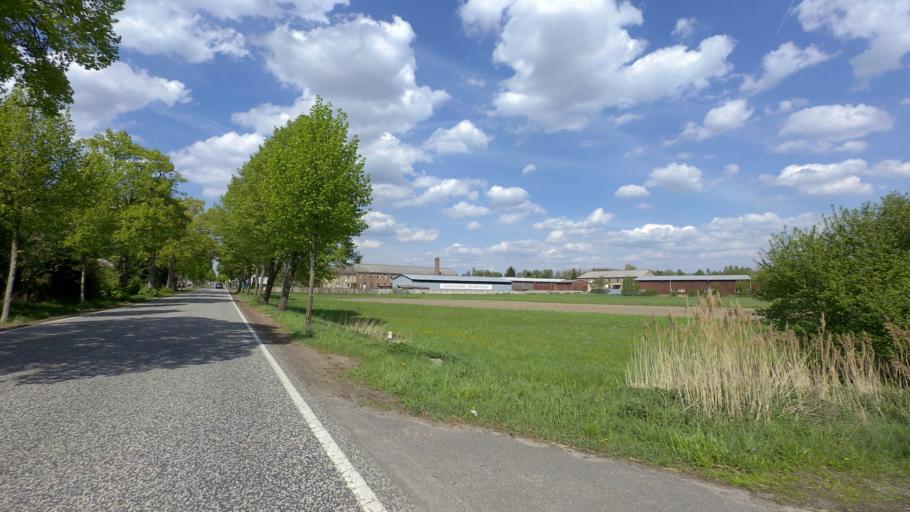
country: DE
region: Brandenburg
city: Marienwerder
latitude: 52.8985
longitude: 13.5368
